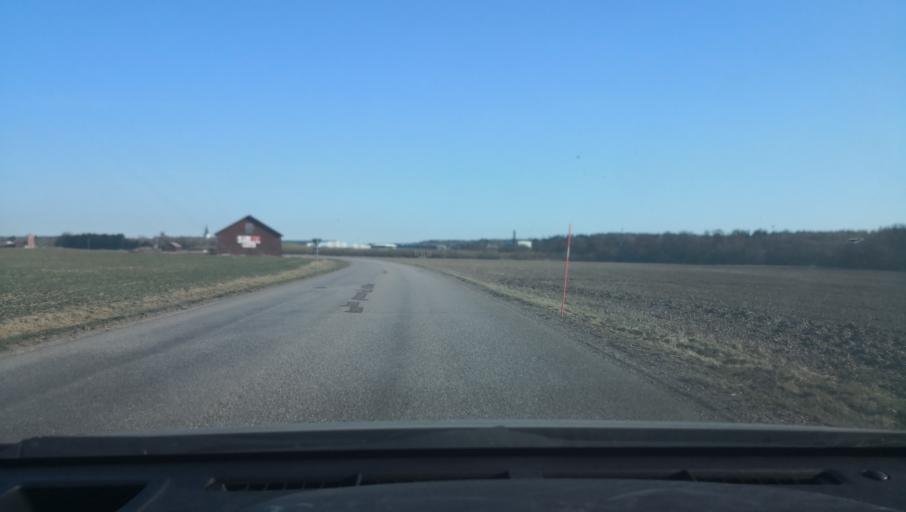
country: SE
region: Uppsala
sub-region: Heby Kommun
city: Heby
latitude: 59.9520
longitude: 16.8392
